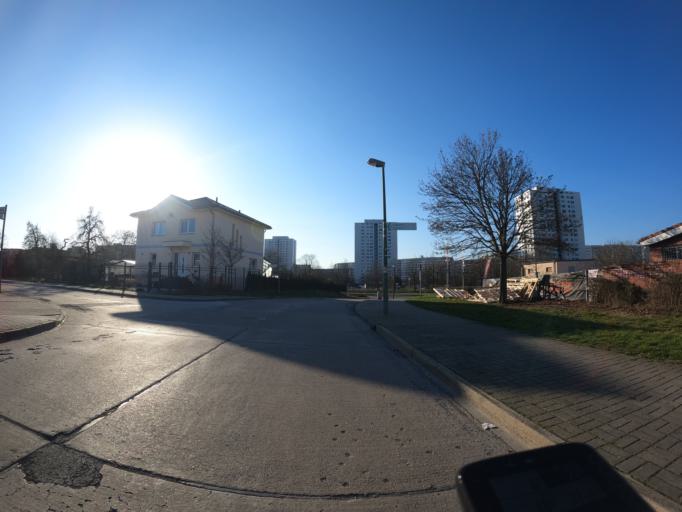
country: DE
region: Berlin
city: Marzahn
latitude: 52.5437
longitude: 13.5552
